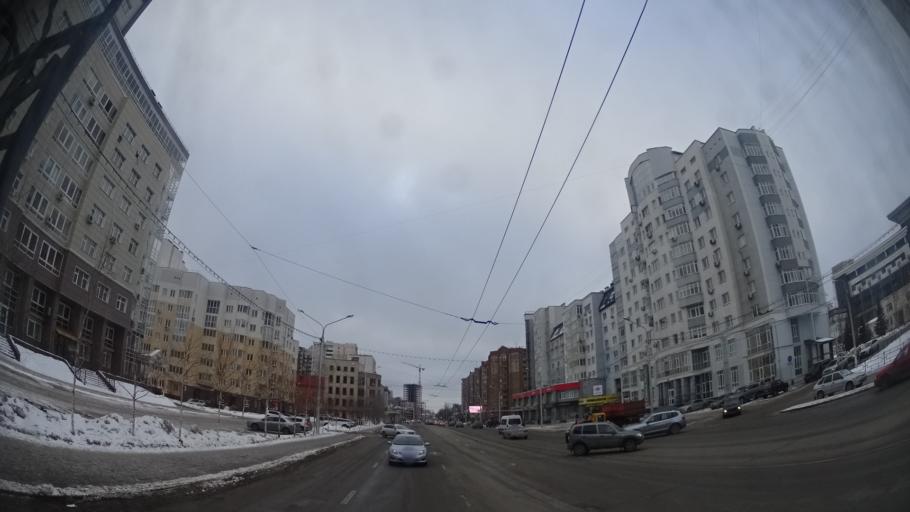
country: RU
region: Bashkortostan
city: Ufa
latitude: 54.7290
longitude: 55.9555
